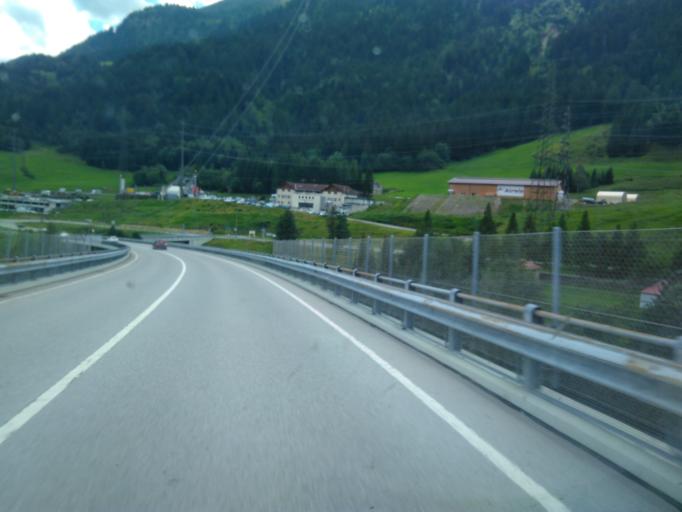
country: CH
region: Ticino
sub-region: Leventina District
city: Airolo
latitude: 46.5265
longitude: 8.5994
